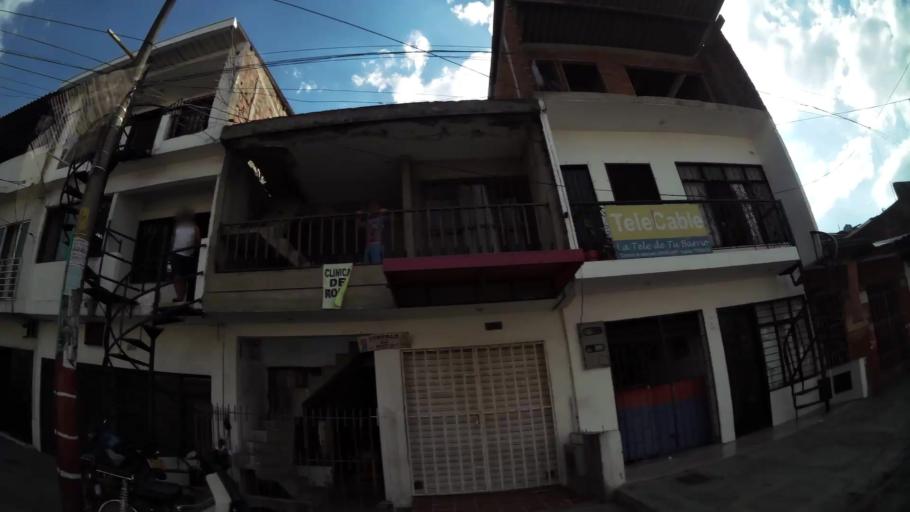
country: CO
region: Valle del Cauca
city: Cali
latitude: 3.4169
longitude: -76.4985
